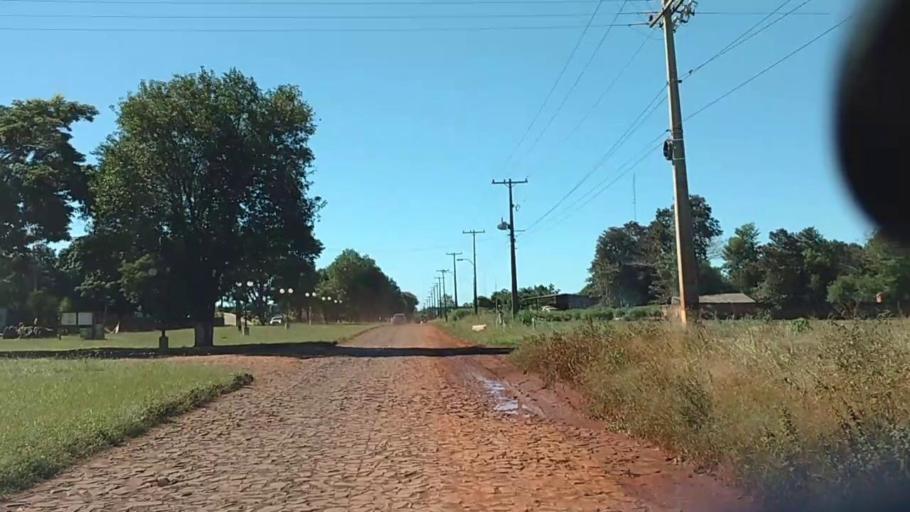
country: PY
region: Alto Parana
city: Naranjal
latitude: -25.9723
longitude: -55.1980
